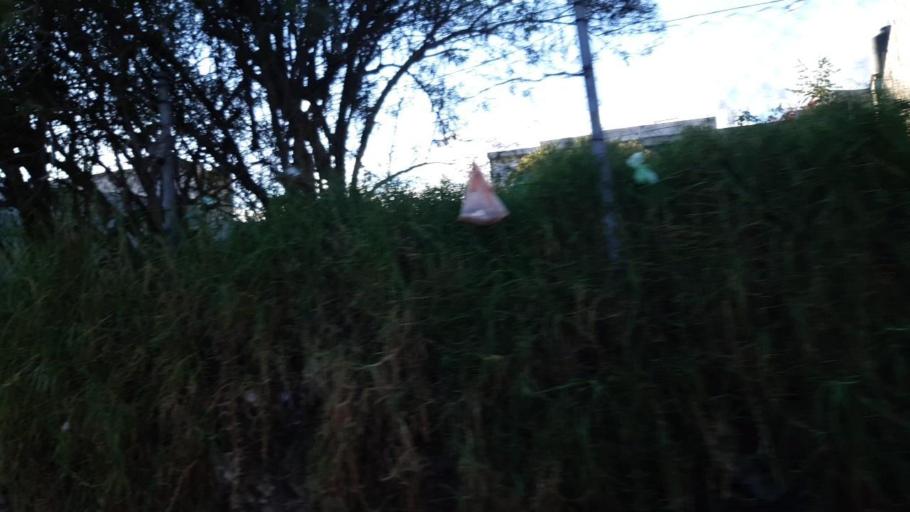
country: GT
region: Quetzaltenango
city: Salcaja
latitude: 14.8785
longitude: -91.4610
